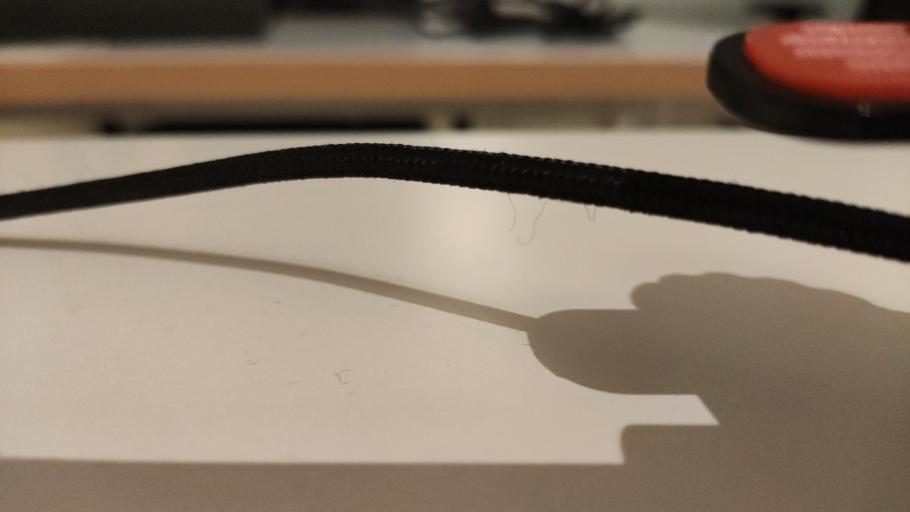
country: RU
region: Moskovskaya
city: Novoye
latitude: 55.6626
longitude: 38.9414
